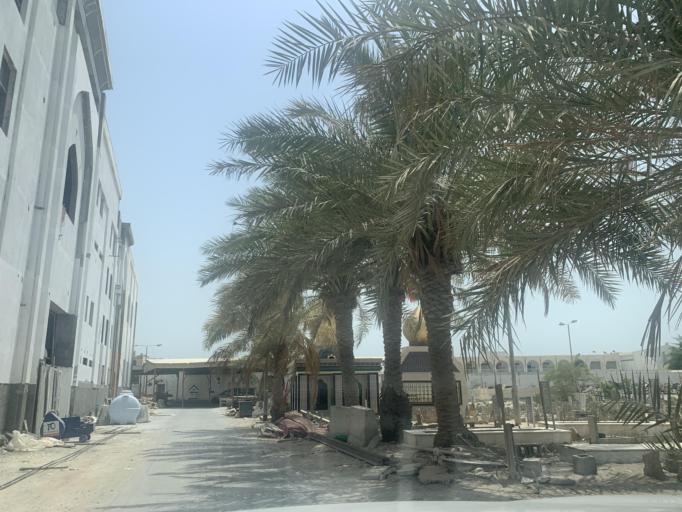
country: BH
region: Manama
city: Jidd Hafs
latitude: 26.2240
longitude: 50.4637
